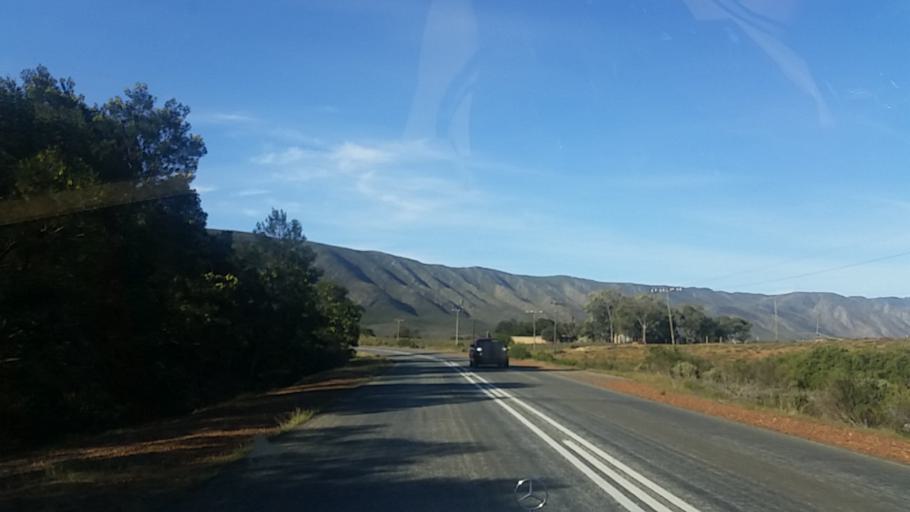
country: ZA
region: Western Cape
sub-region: Eden District Municipality
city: Knysna
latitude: -33.7719
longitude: 22.9606
